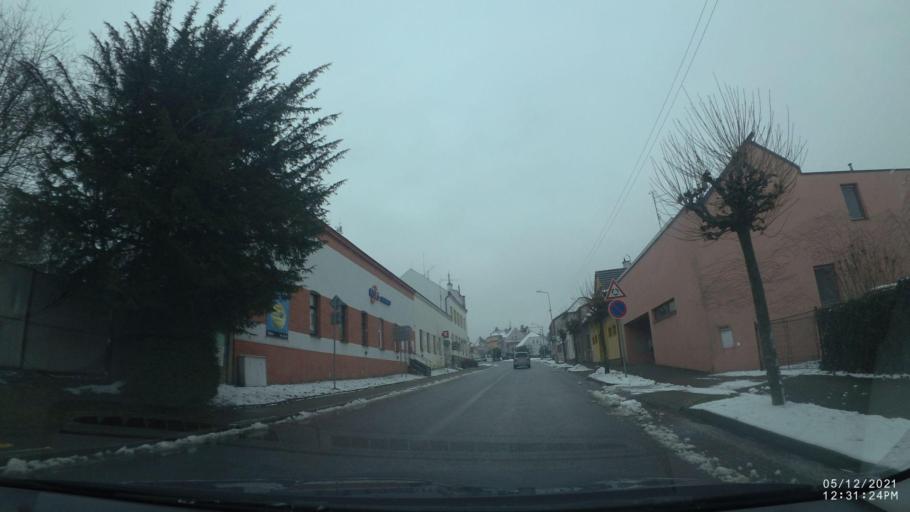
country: CZ
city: Nove Mesto nad Metuji
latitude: 50.3542
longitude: 16.1481
